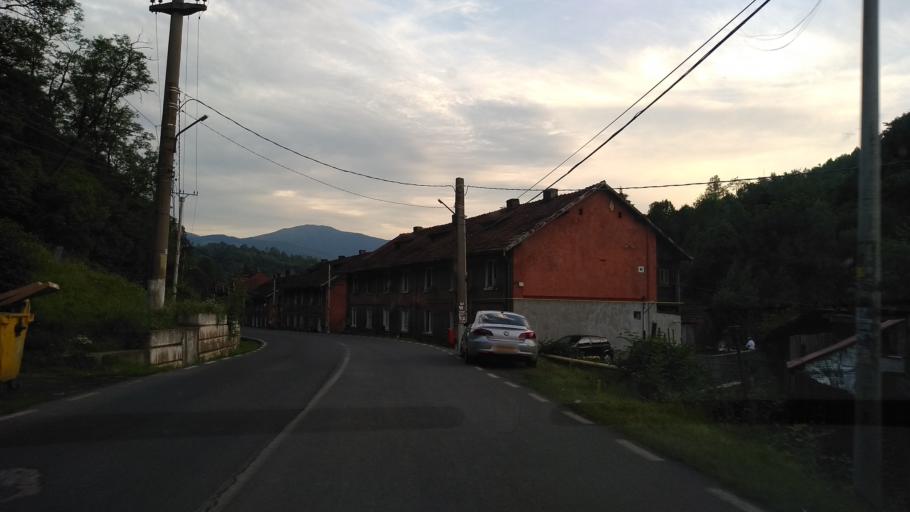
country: RO
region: Hunedoara
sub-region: Comuna Aninoasa
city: Aninoasa
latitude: 45.4017
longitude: 23.3208
